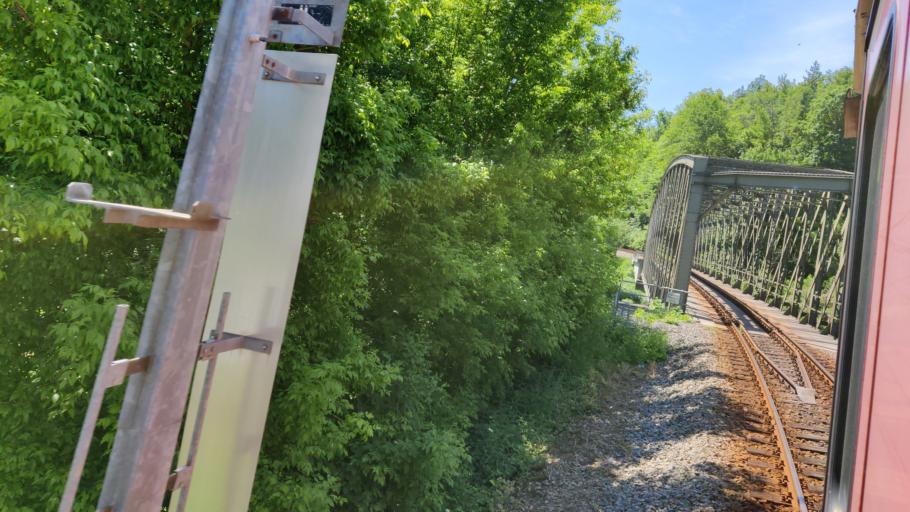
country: AT
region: Lower Austria
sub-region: Politischer Bezirk Horn
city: Horn
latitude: 48.6272
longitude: 15.6421
